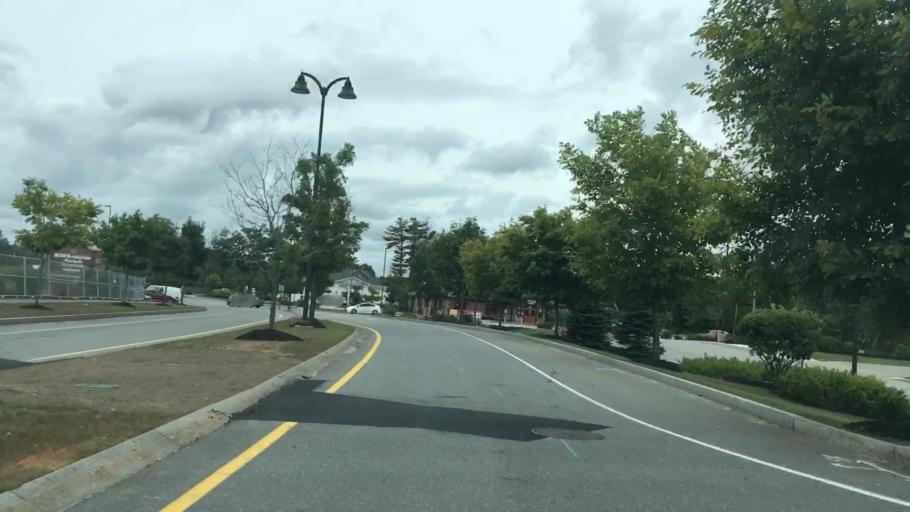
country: US
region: Maine
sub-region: Cumberland County
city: South Portland Gardens
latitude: 43.6245
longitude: -70.3413
